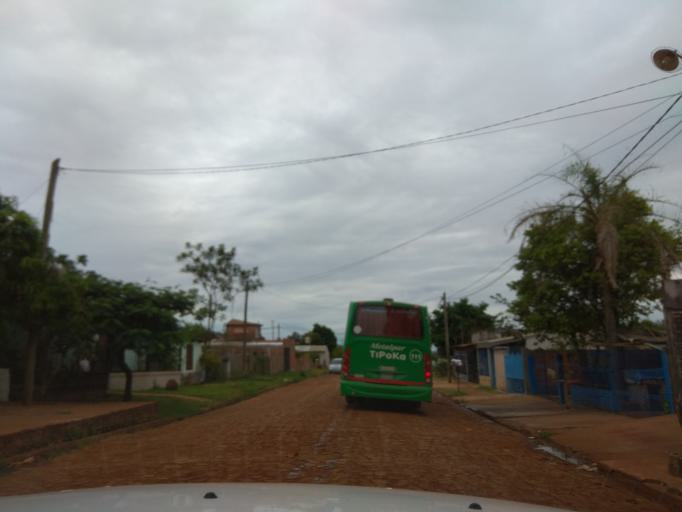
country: AR
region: Misiones
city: Garupa
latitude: -27.4391
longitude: -55.8609
